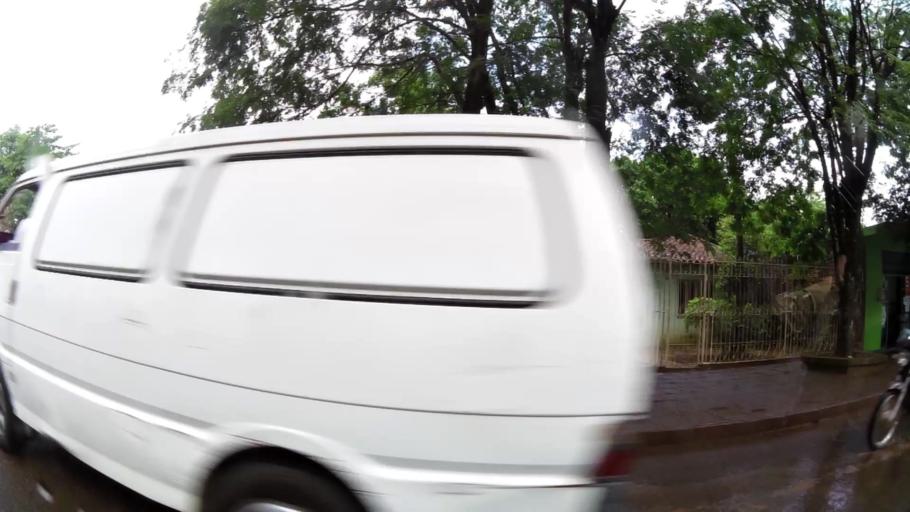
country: PY
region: Alto Parana
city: Presidente Franco
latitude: -25.5198
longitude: -54.6665
